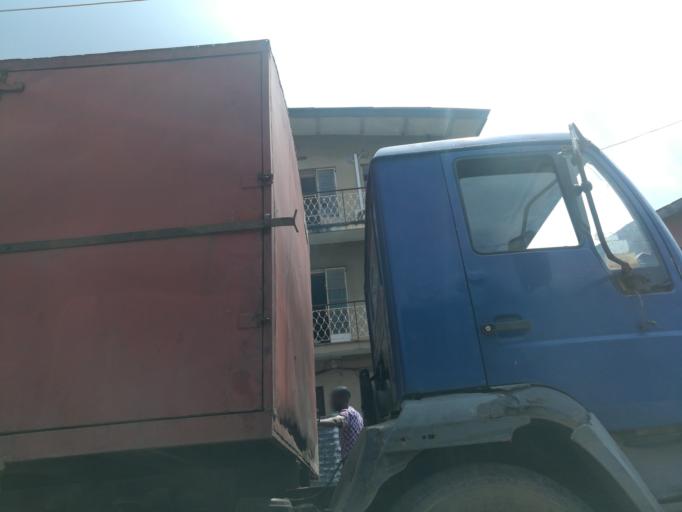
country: NG
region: Lagos
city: Somolu
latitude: 6.5382
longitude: 3.3639
